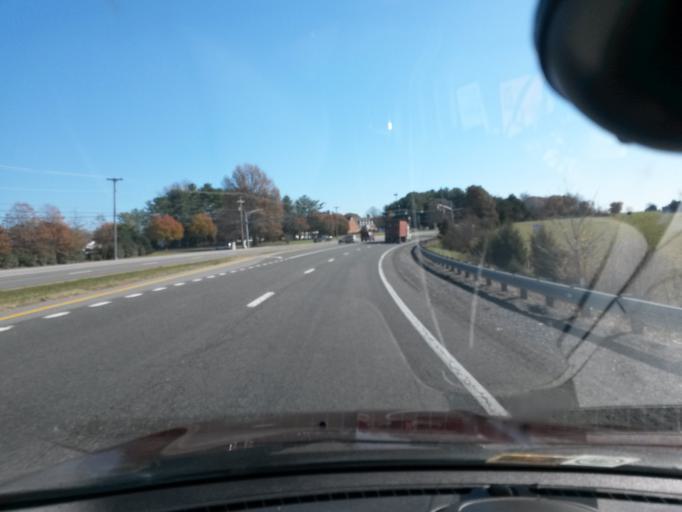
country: US
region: Virginia
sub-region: City of Bedford
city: Bedford
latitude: 37.3195
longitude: -79.4854
